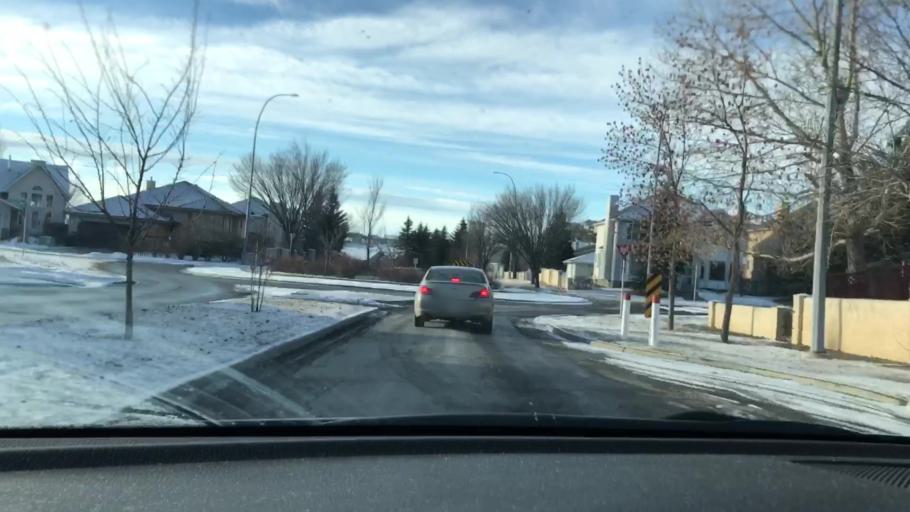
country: CA
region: Alberta
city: Calgary
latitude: 51.0205
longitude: -114.1831
